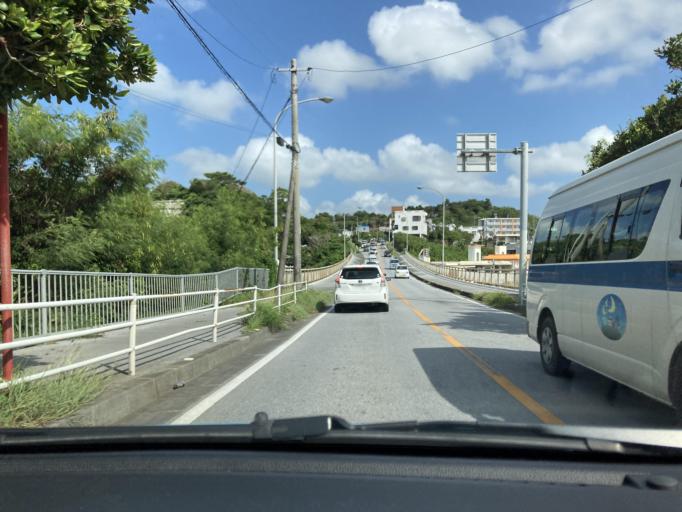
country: JP
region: Okinawa
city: Chatan
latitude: 26.2935
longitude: 127.7846
